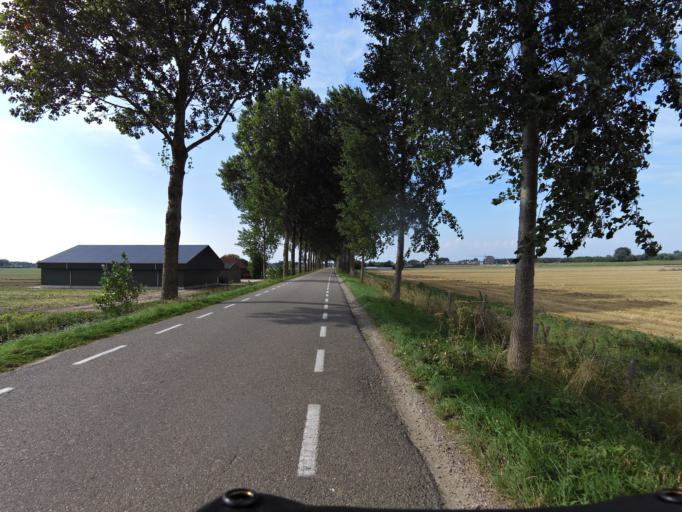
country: NL
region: South Holland
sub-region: Gemeente Zwijndrecht
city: Heerjansdam
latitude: 51.7969
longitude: 4.5844
